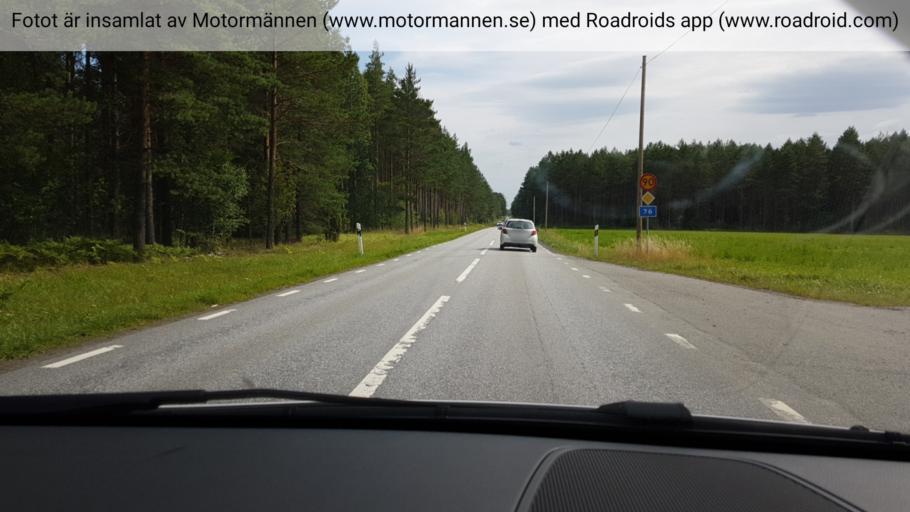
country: SE
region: Uppsala
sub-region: Osthammars Kommun
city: Anneberg
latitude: 60.1960
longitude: 18.3792
